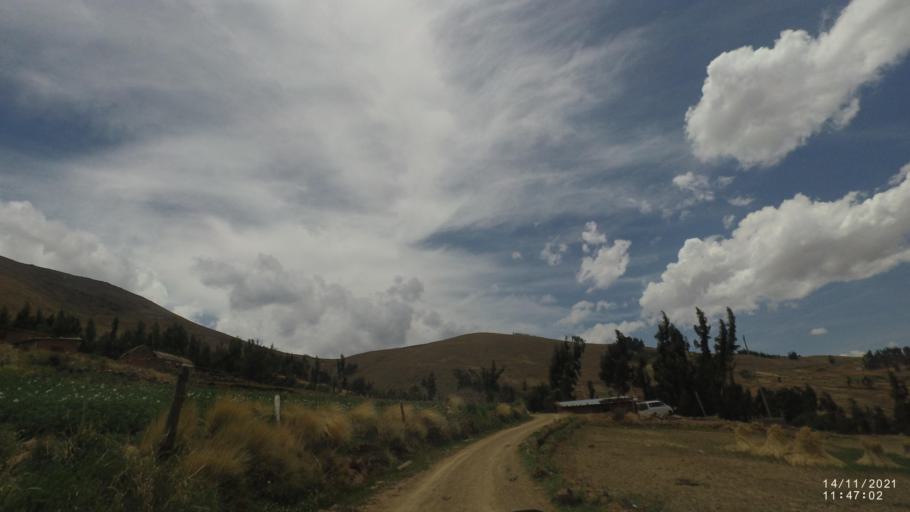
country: BO
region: Cochabamba
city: Colomi
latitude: -17.3528
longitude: -65.9861
